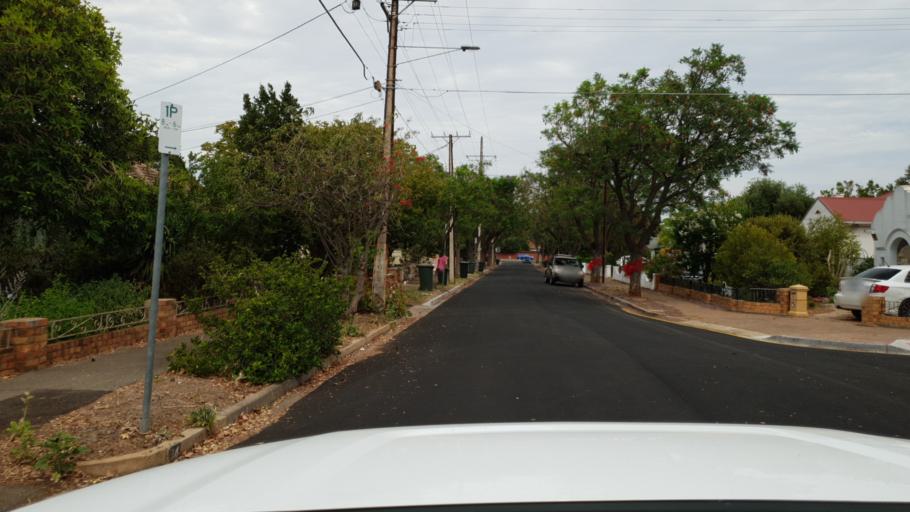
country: AU
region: South Australia
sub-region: Mitcham
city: Clarence Gardens
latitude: -34.9696
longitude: 138.5752
